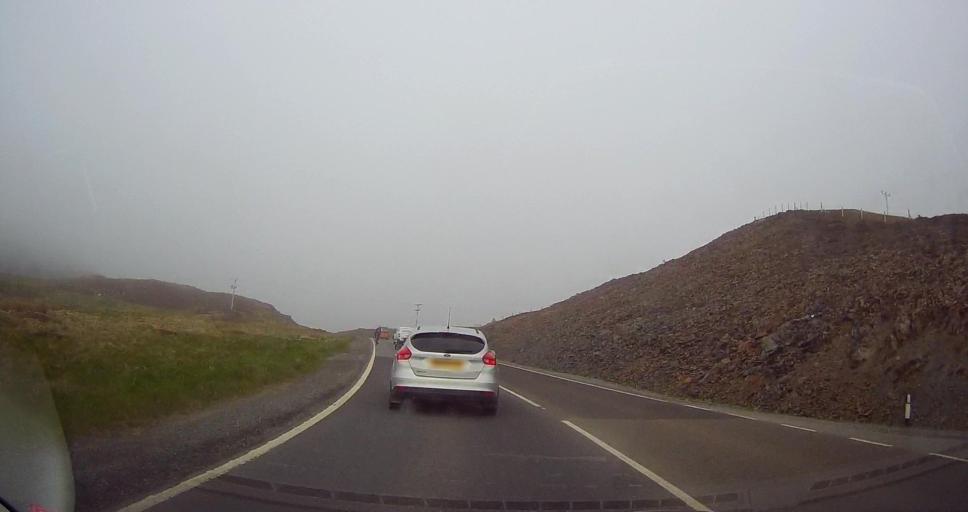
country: GB
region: Scotland
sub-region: Shetland Islands
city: Lerwick
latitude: 60.1392
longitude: -1.2604
